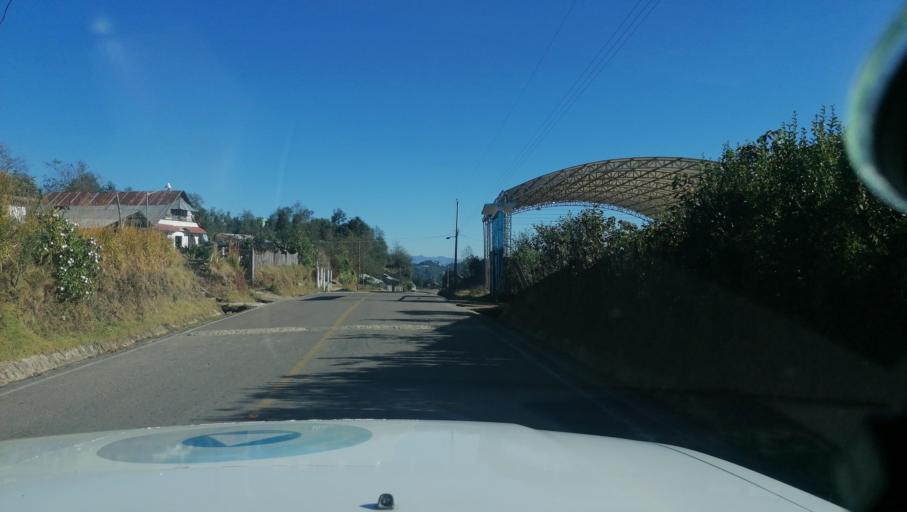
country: MX
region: Chiapas
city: Motozintla de Mendoza
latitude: 15.2398
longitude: -92.2306
